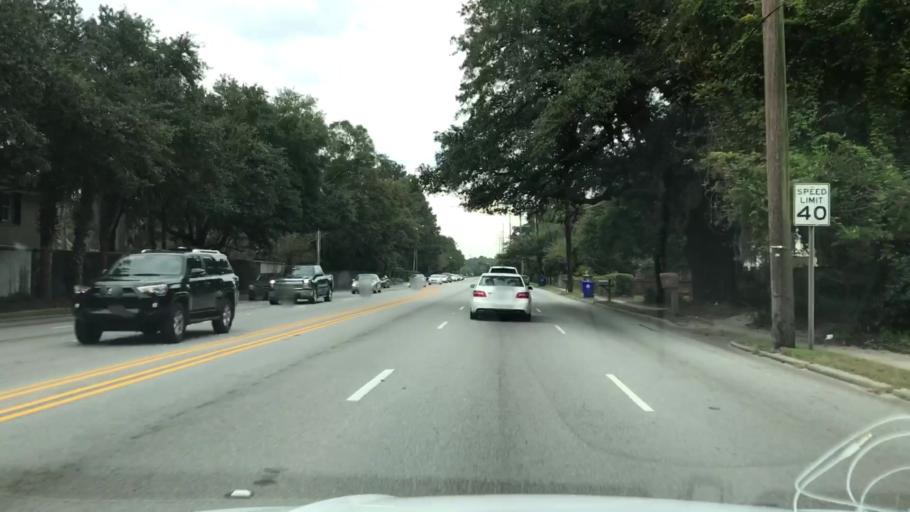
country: US
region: South Carolina
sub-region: Charleston County
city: Charleston
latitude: 32.7737
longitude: -79.9738
